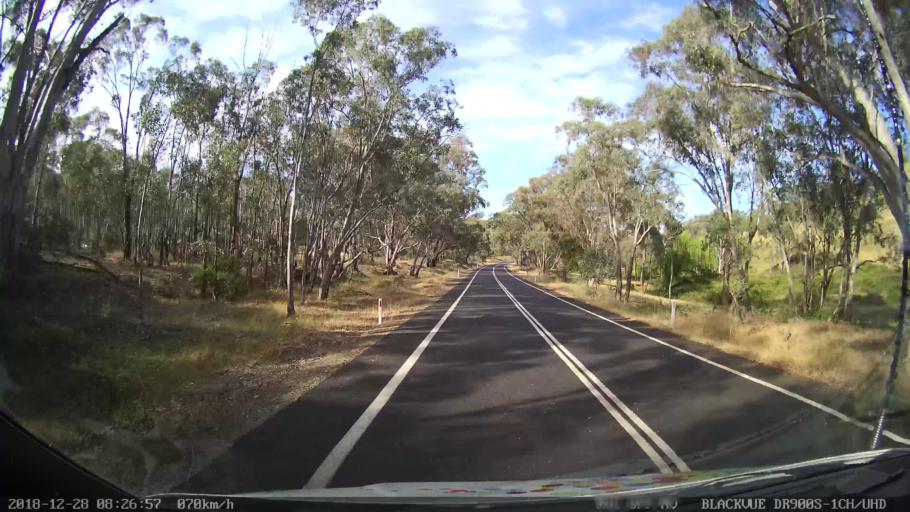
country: AU
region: New South Wales
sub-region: Blayney
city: Blayney
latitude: -33.9395
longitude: 149.3420
